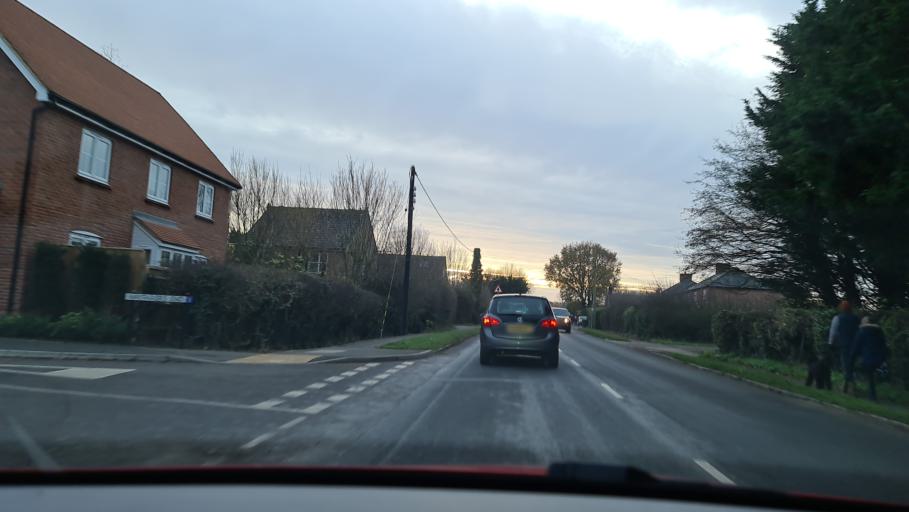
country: GB
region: England
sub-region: Buckinghamshire
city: Princes Risborough
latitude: 51.7401
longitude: -0.8620
